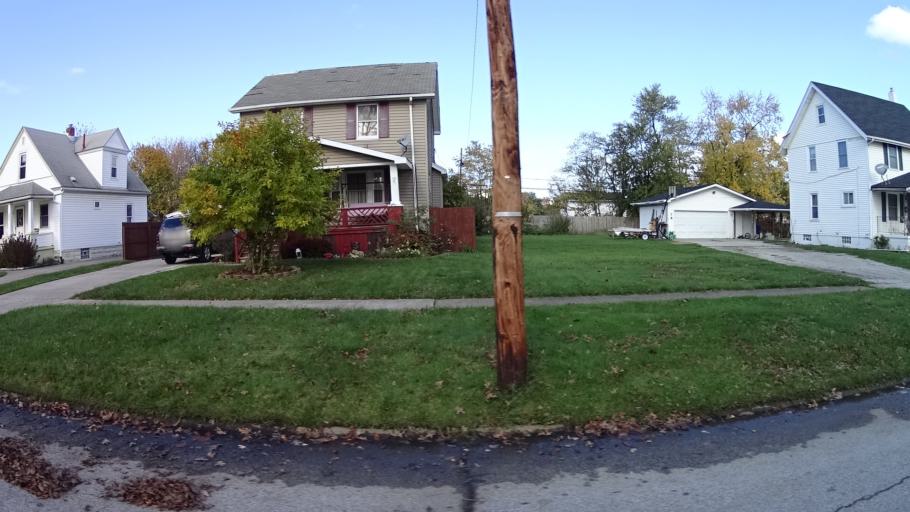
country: US
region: Ohio
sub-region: Lorain County
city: Lorain
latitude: 41.4399
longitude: -82.1433
